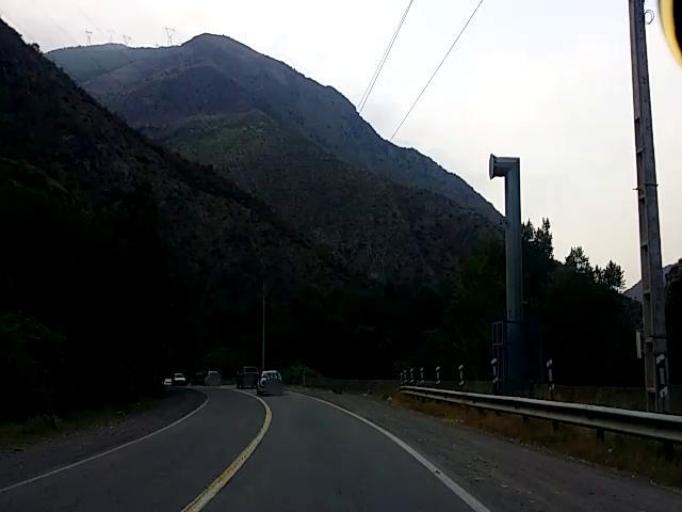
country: IR
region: Mazandaran
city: Chalus
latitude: 36.3447
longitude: 51.2579
